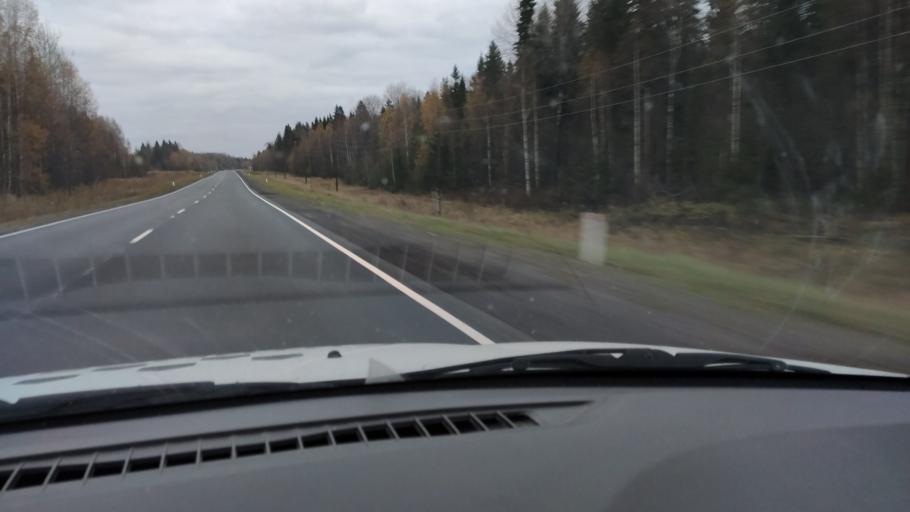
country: RU
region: Kirov
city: Lesnyye Polyany
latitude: 58.8290
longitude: 52.6375
